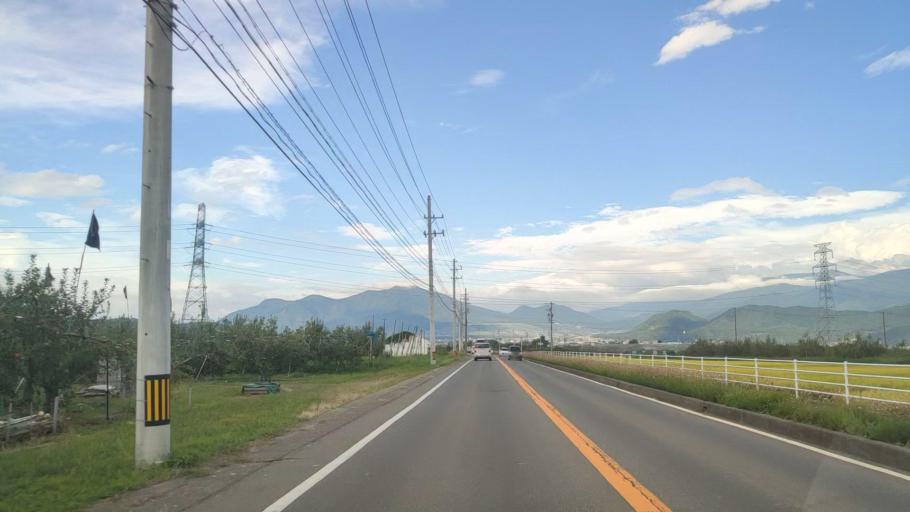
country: JP
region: Nagano
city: Nakano
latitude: 36.7198
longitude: 138.3281
